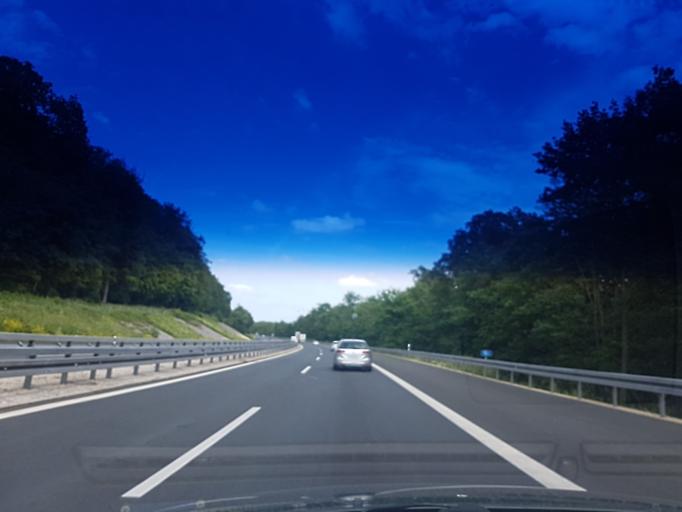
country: DE
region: Bavaria
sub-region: Upper Franconia
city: Schesslitz
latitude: 49.9690
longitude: 11.0088
